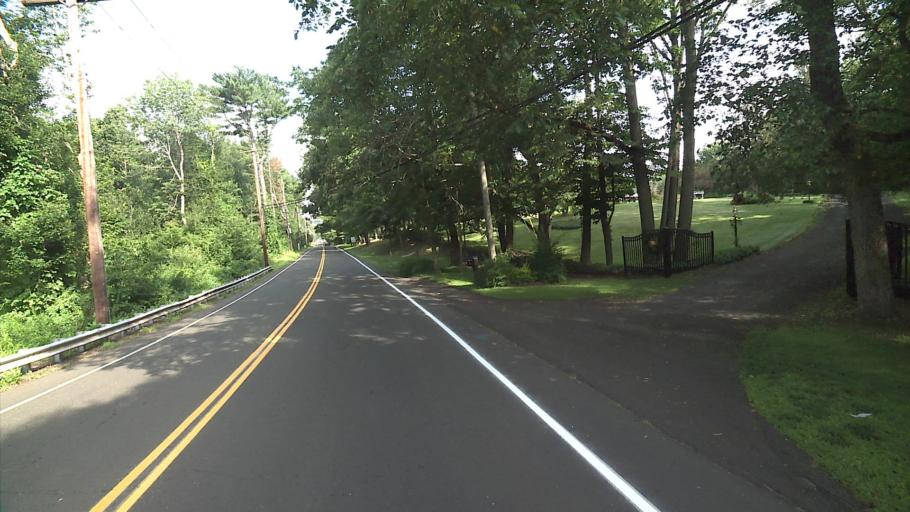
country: US
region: Connecticut
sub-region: New Haven County
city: Woodbridge
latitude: 41.3316
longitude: -72.9951
